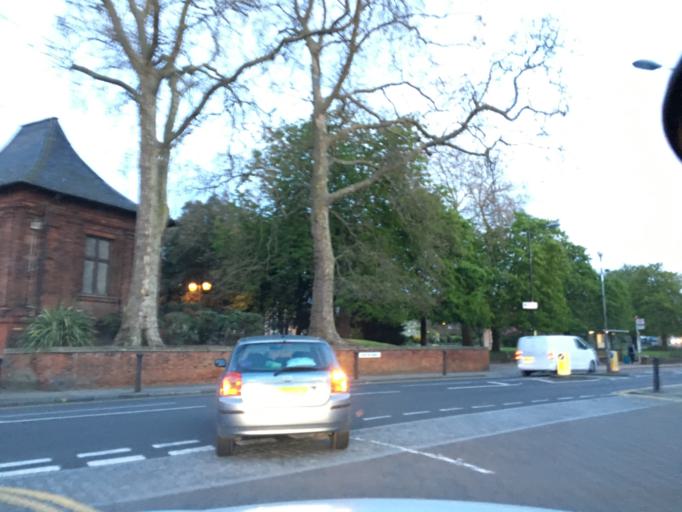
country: GB
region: England
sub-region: Greater London
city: Woolwich
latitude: 51.4813
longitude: 0.0358
